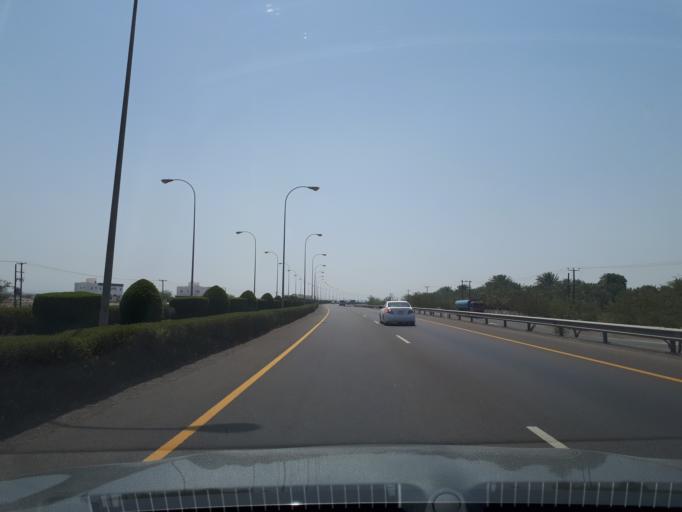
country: OM
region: Al Batinah
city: Al Sohar
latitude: 24.4111
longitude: 56.6422
